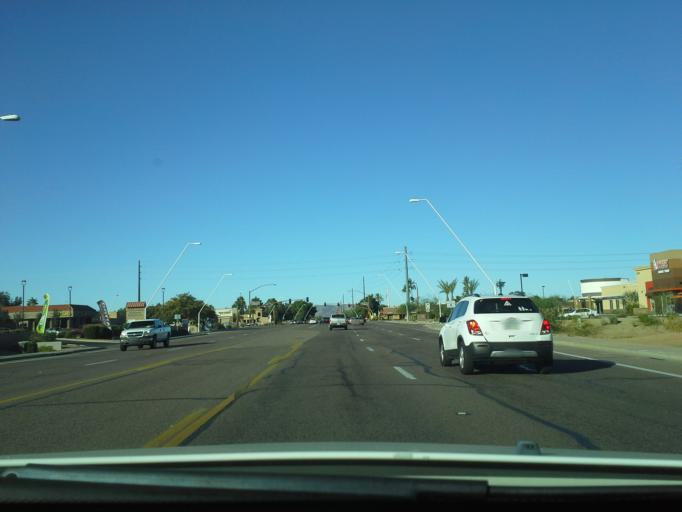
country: US
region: Arizona
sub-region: Maricopa County
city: San Carlos
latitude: 33.3496
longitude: -111.8742
